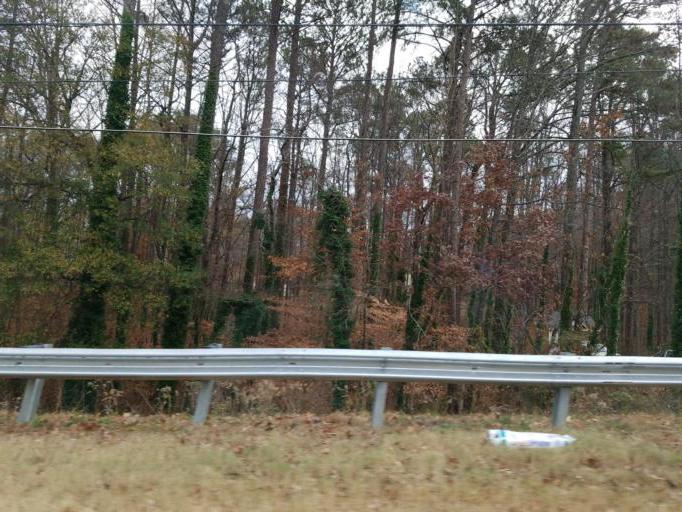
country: US
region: Georgia
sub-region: Cherokee County
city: Canton
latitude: 34.2121
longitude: -84.5249
